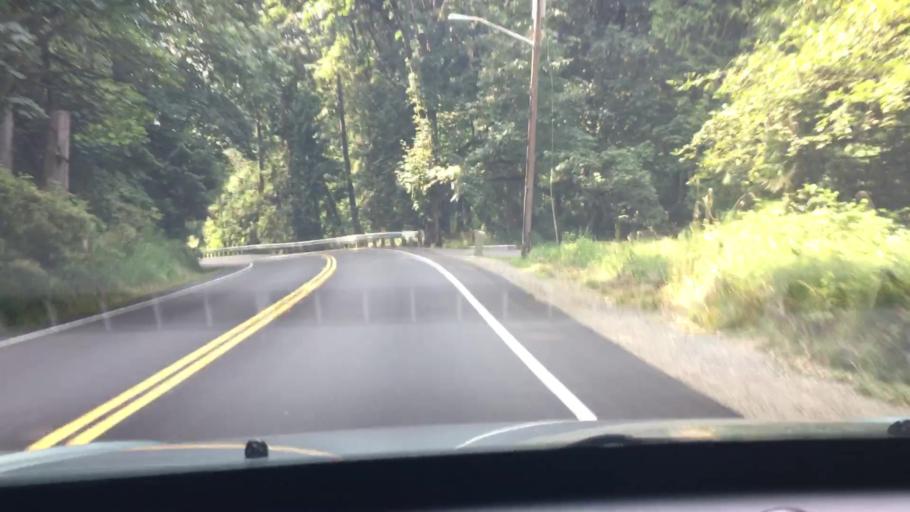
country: US
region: Washington
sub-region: King County
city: City of Sammamish
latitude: 47.5724
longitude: -122.0604
